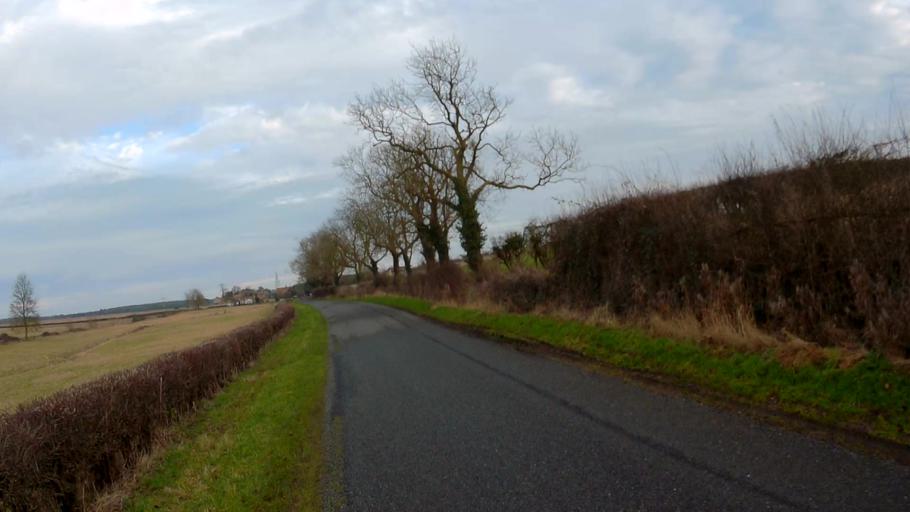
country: GB
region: England
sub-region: Lincolnshire
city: Bourne
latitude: 52.8338
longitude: -0.4557
